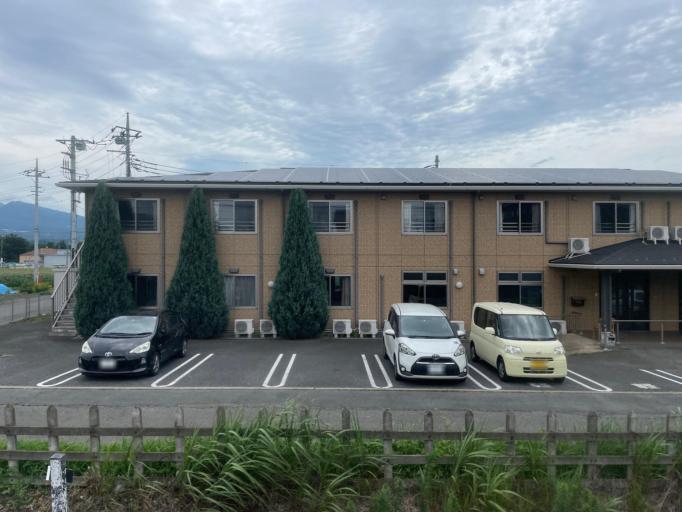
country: JP
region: Gunma
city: Kanekomachi
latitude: 36.4319
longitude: 139.0289
